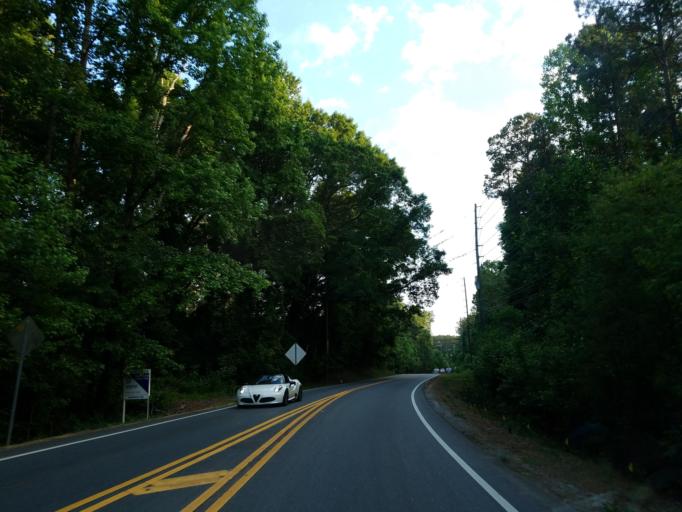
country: US
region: Georgia
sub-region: Cherokee County
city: Holly Springs
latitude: 34.1862
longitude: -84.5434
